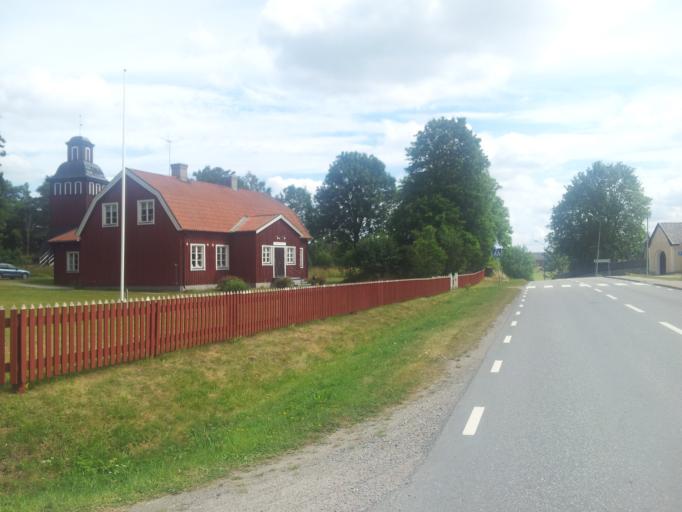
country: SE
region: Stockholm
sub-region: Norrtalje Kommun
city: Nykvarn
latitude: 59.9093
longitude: 18.2677
